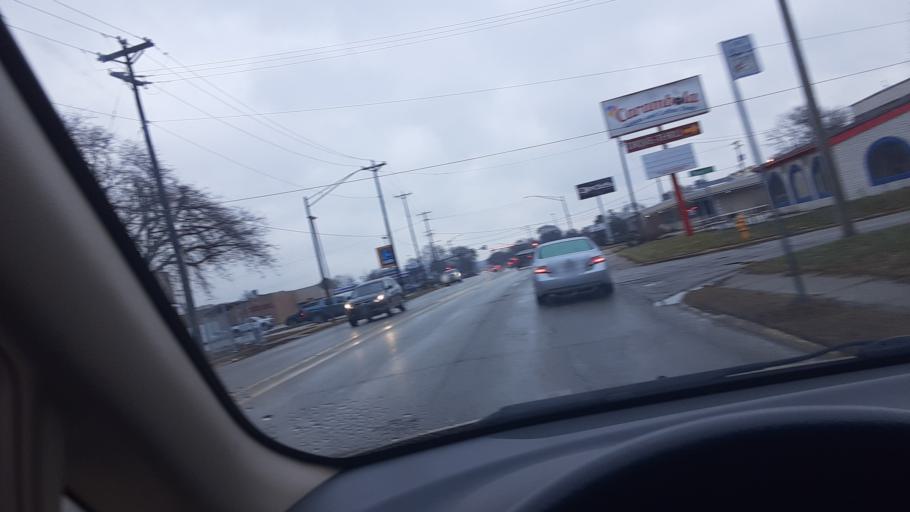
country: US
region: Illinois
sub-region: Winnebago County
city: Loves Park
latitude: 42.3161
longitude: -89.0603
